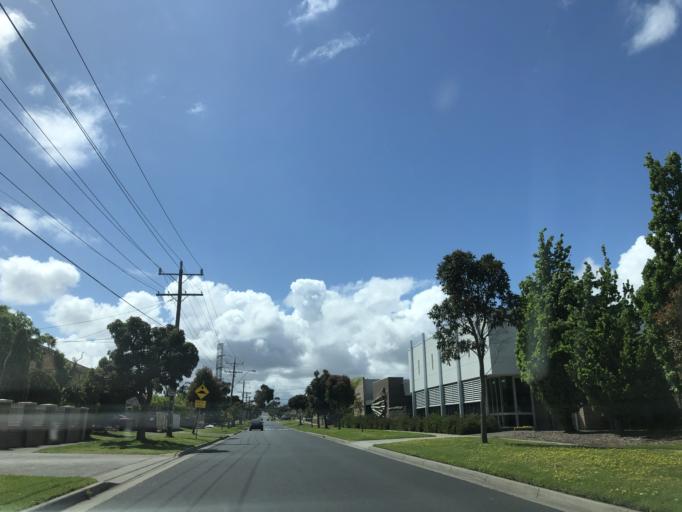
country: AU
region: Victoria
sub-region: Kingston
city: Clayton South
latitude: -37.9408
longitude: 145.1018
